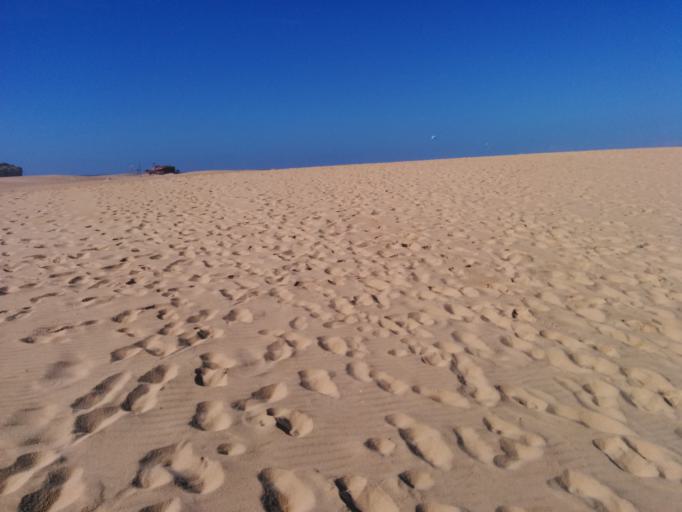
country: PT
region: Faro
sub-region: Vila do Bispo
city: Vila do Bispo
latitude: 37.1952
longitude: -8.9016
